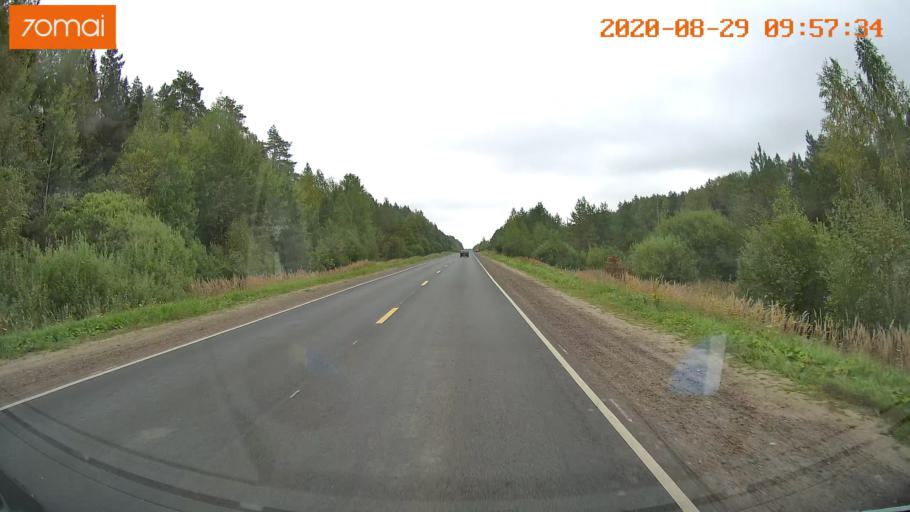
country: RU
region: Ivanovo
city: Zarechnyy
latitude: 57.4161
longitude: 42.3171
